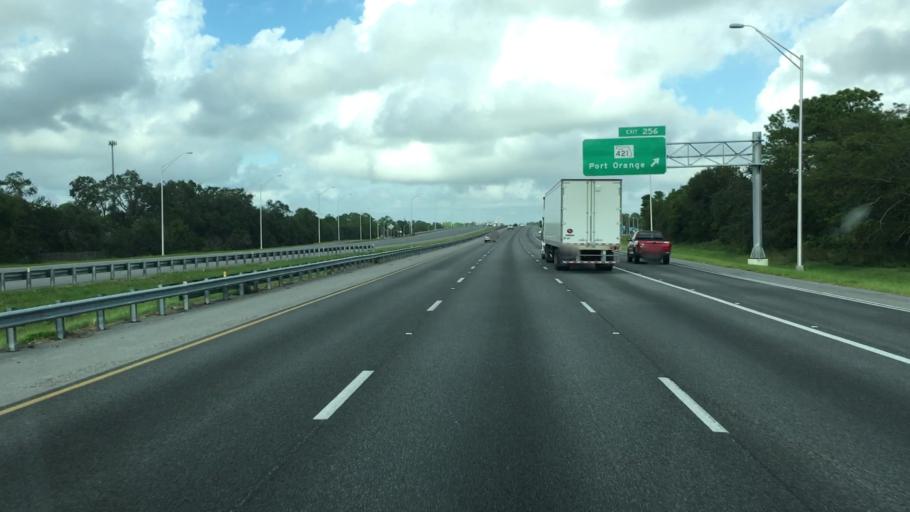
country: US
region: Florida
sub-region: Volusia County
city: Port Orange
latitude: 29.1005
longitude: -81.0257
